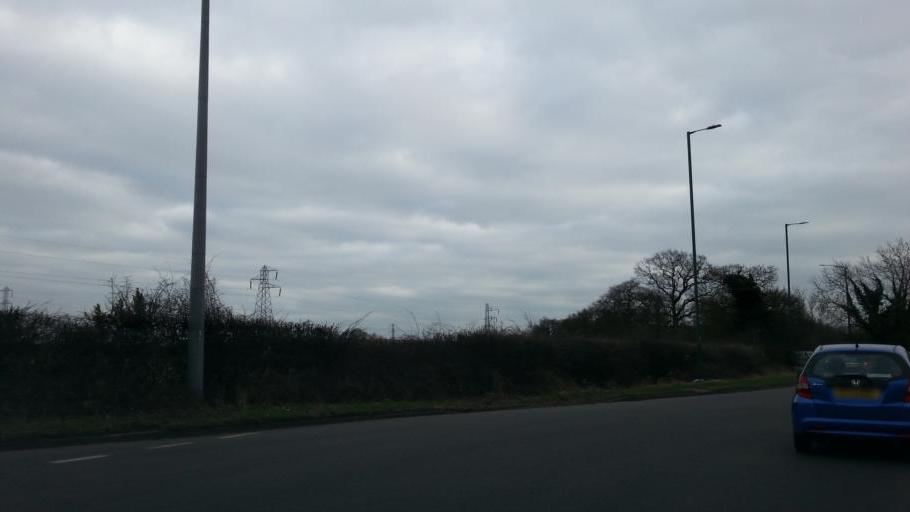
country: GB
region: England
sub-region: Solihull
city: Chelmsley Wood
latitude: 52.4751
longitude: -1.7218
